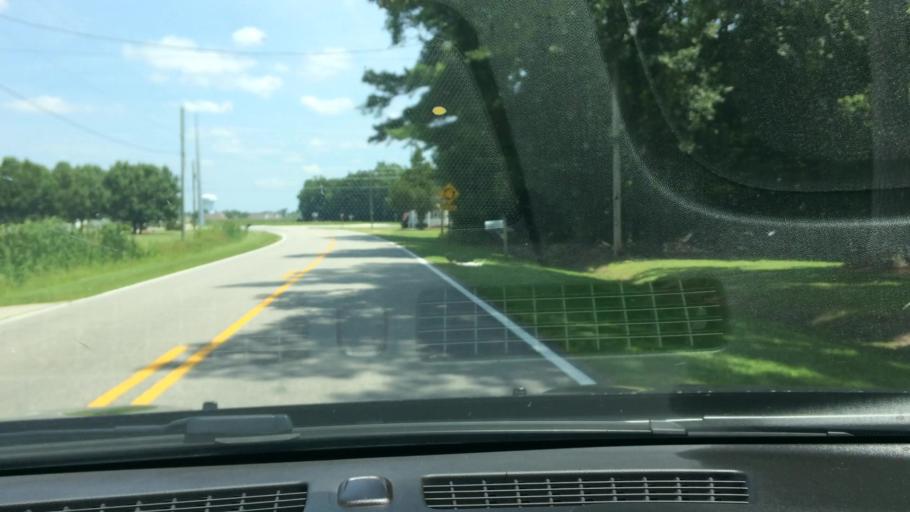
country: US
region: North Carolina
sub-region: Pitt County
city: Windsor
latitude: 35.5221
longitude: -77.3075
